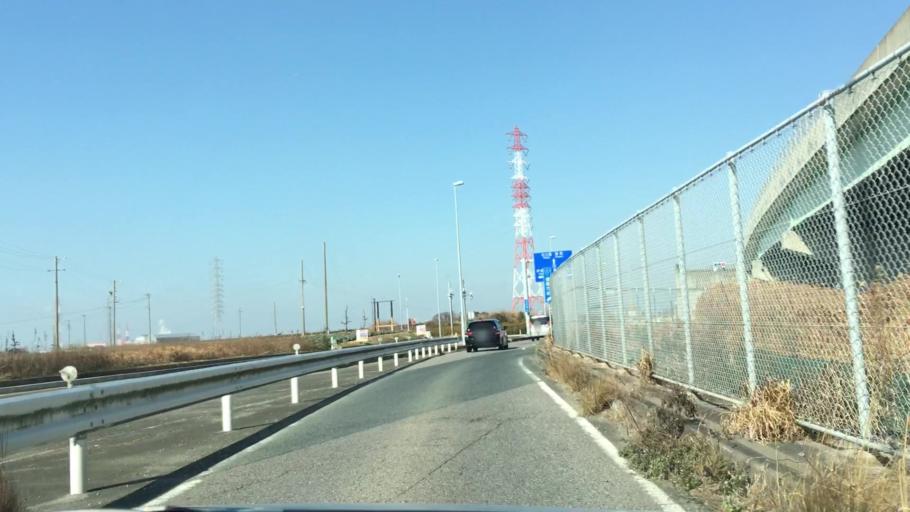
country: JP
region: Aichi
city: Toyohashi
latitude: 34.7068
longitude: 137.3541
